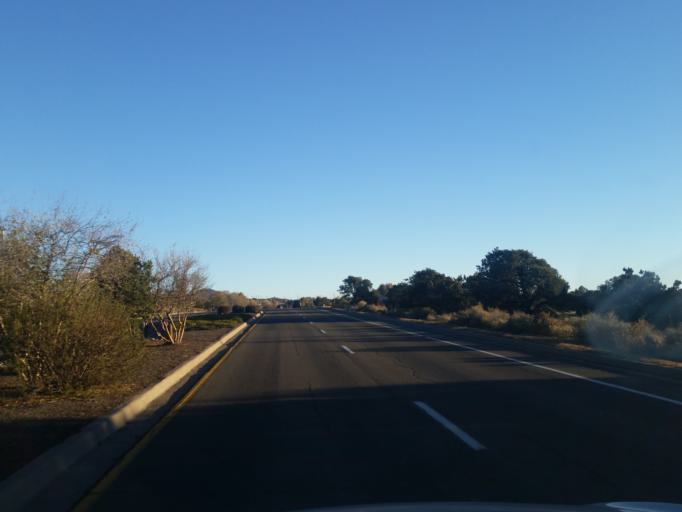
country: US
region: New Mexico
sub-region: Santa Fe County
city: Santa Fe
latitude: 35.6489
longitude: -105.9349
